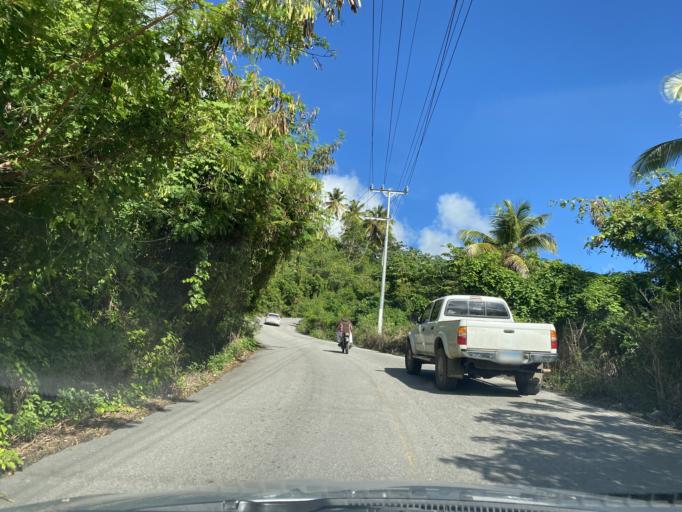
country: DO
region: Samana
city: Sanchez
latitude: 19.2350
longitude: -69.5973
